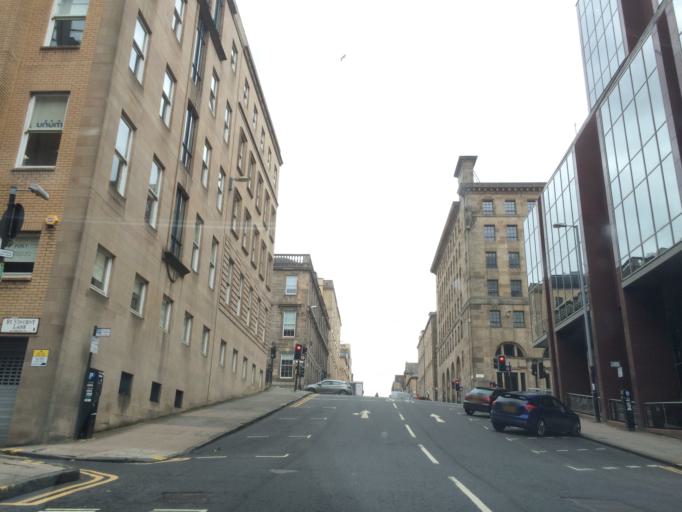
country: GB
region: Scotland
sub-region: Glasgow City
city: Glasgow
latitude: 55.8615
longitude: -4.2616
